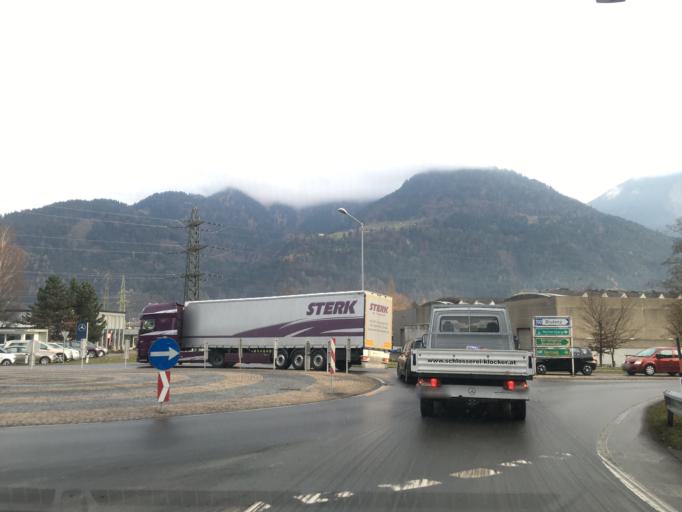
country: AT
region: Vorarlberg
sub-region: Politischer Bezirk Bludenz
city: Nuziders
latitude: 47.1660
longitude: 9.7920
